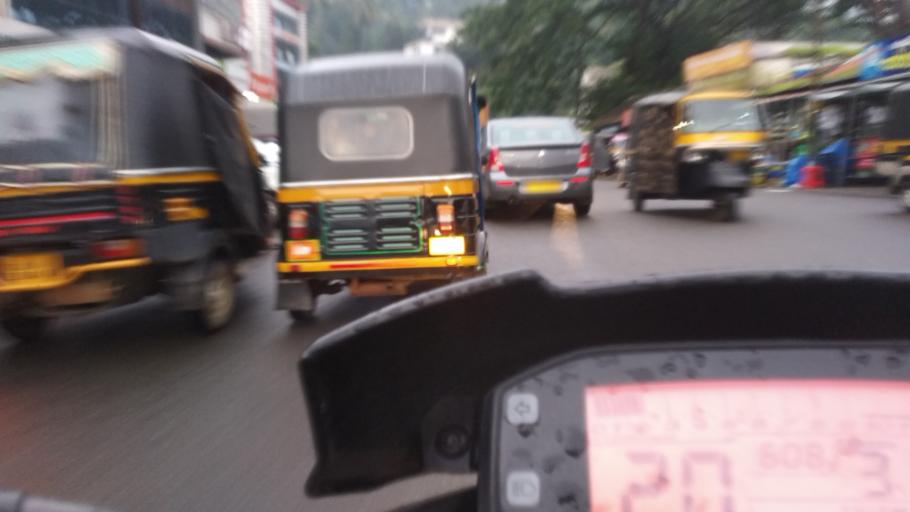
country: IN
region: Kerala
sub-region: Idukki
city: Munnar
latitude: 10.0142
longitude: 76.9562
